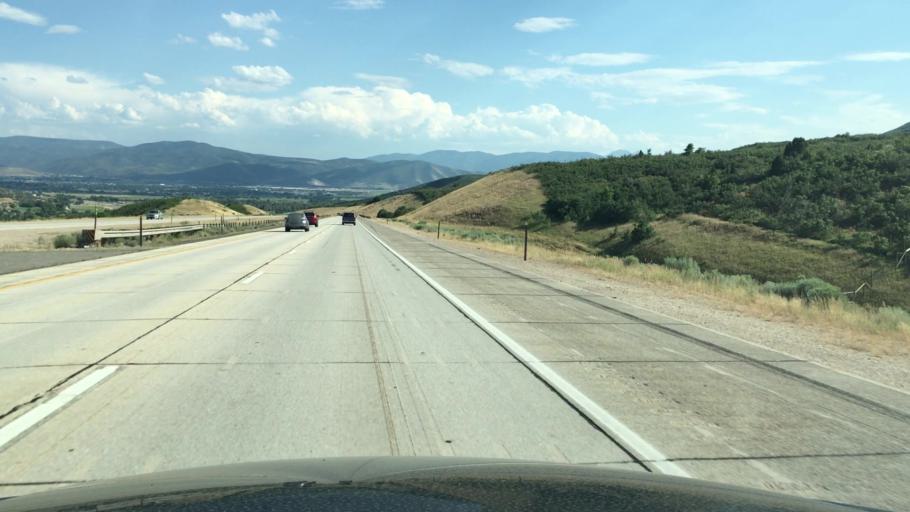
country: US
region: Utah
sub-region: Wasatch County
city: Heber
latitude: 40.5855
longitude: -111.4367
